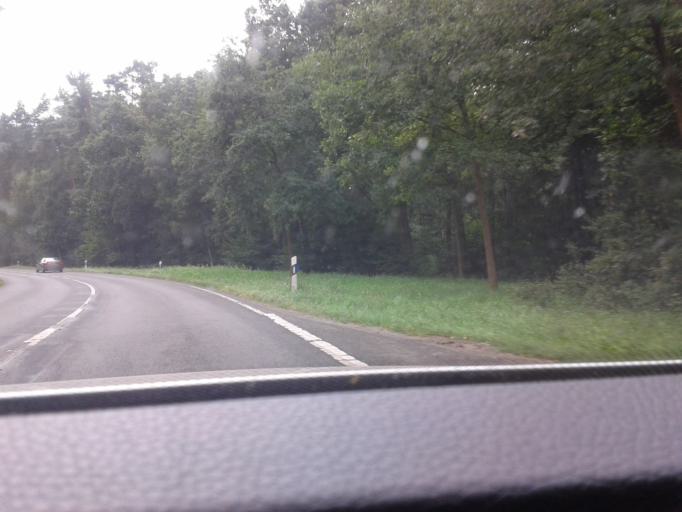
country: DE
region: Lower Saxony
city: Gifhorn
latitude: 52.4955
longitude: 10.5691
